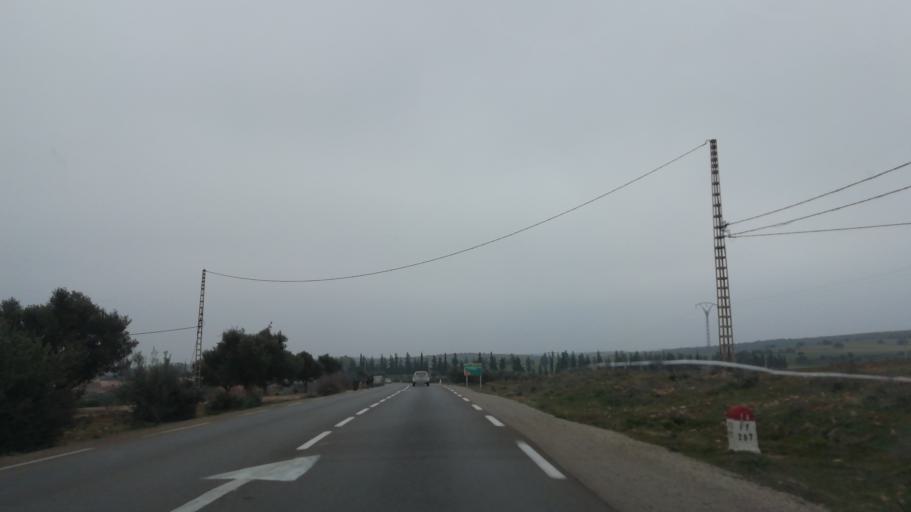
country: DZ
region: Mascara
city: Mascara
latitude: 35.3087
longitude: 0.4041
